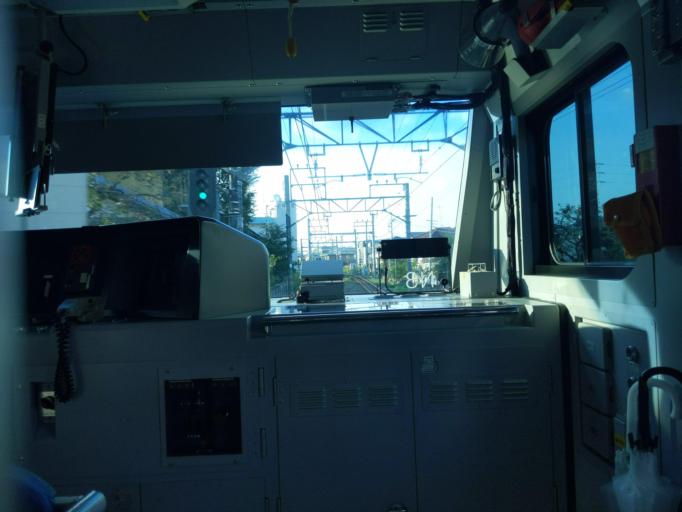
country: JP
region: Tokyo
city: Chofugaoka
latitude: 35.6129
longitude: 139.5881
